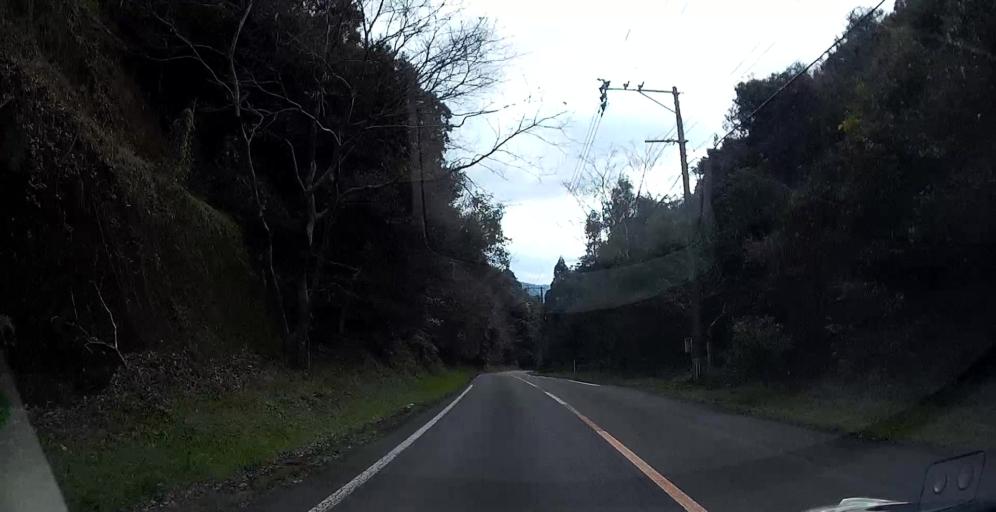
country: JP
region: Kumamoto
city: Yatsushiro
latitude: 32.3718
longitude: 130.5046
